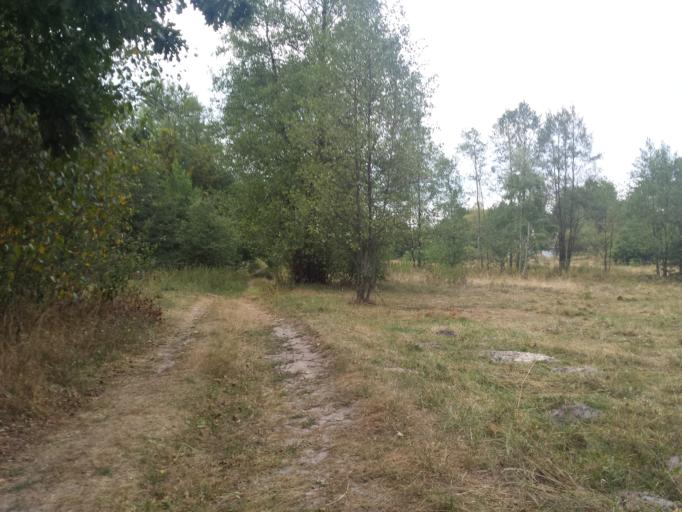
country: PL
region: Swietokrzyskie
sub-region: Powiat staszowski
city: Staszow
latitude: 50.6642
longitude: 21.1555
